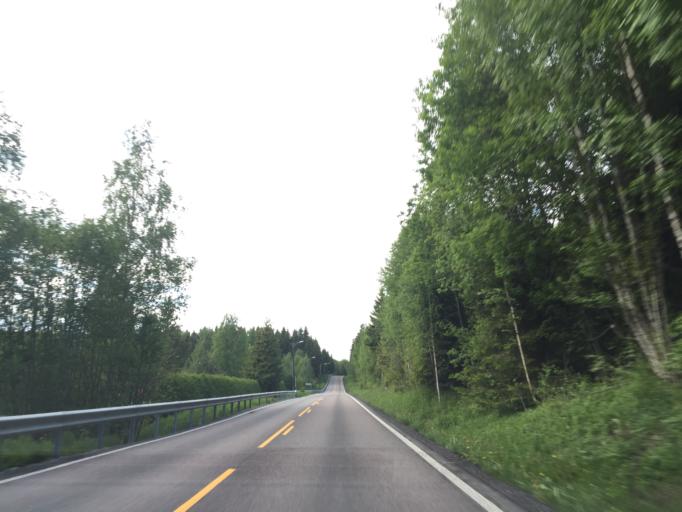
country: NO
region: Akershus
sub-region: Sorum
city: Sorumsand
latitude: 59.9530
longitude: 11.2033
